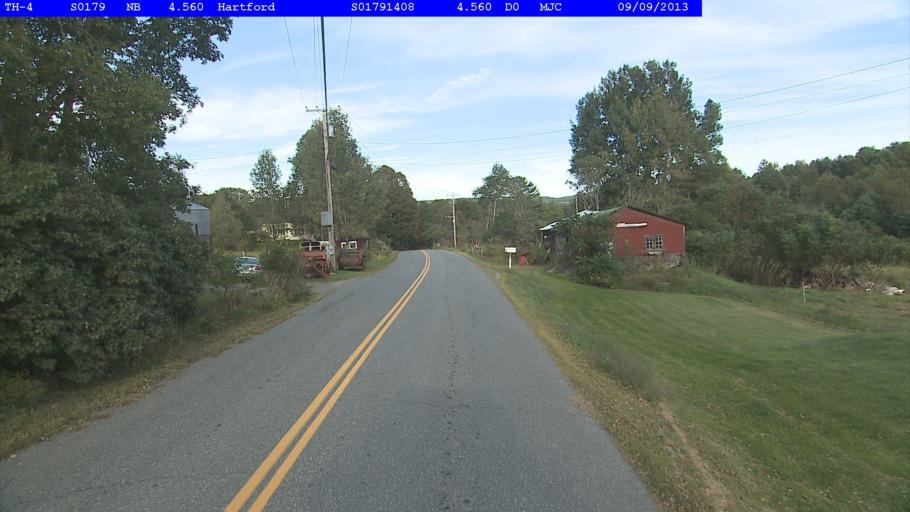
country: US
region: Vermont
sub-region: Windsor County
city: Woodstock
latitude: 43.7004
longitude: -72.4275
